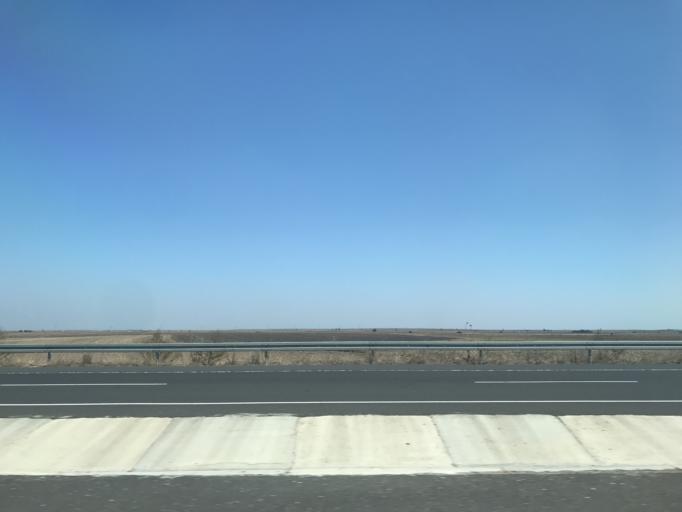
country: TR
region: Tekirdag
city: Muratli
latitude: 41.1908
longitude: 27.5396
